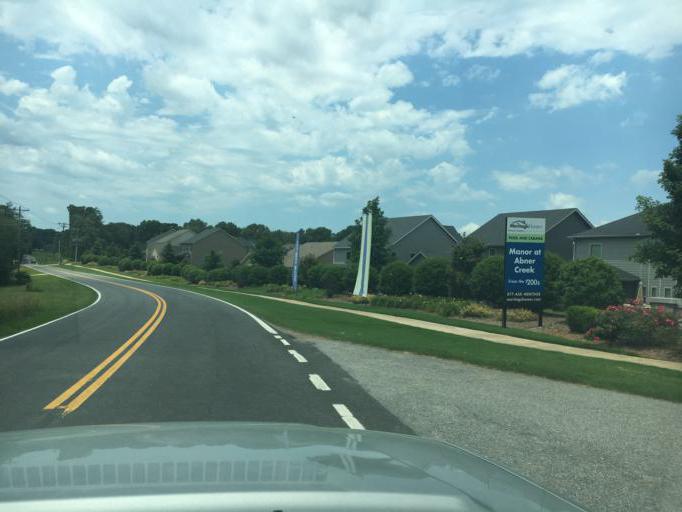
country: US
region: South Carolina
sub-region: Spartanburg County
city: Duncan
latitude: 34.8751
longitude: -82.1713
